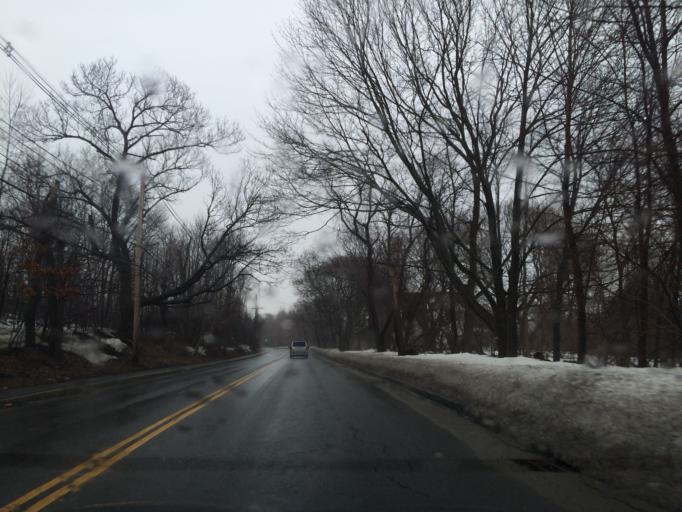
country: US
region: Massachusetts
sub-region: Middlesex County
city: Belmont
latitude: 42.3976
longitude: -71.2103
